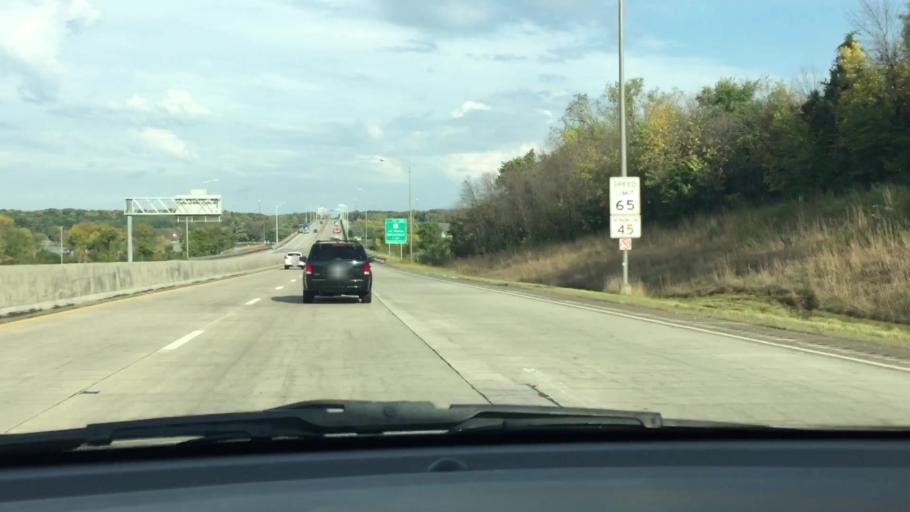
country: US
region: Iowa
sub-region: Scott County
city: Le Claire
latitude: 41.5739
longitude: -90.3610
